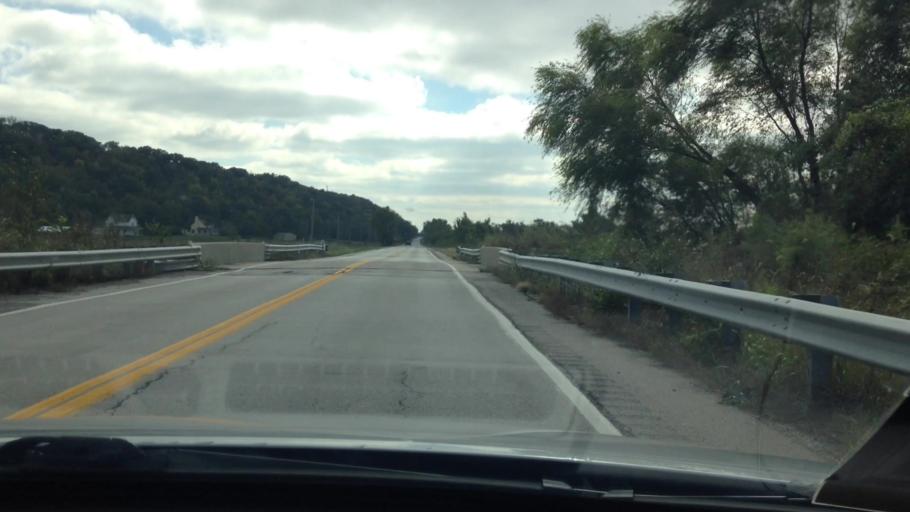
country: US
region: Kansas
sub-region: Leavenworth County
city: Lansing
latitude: 39.2539
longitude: -94.8072
